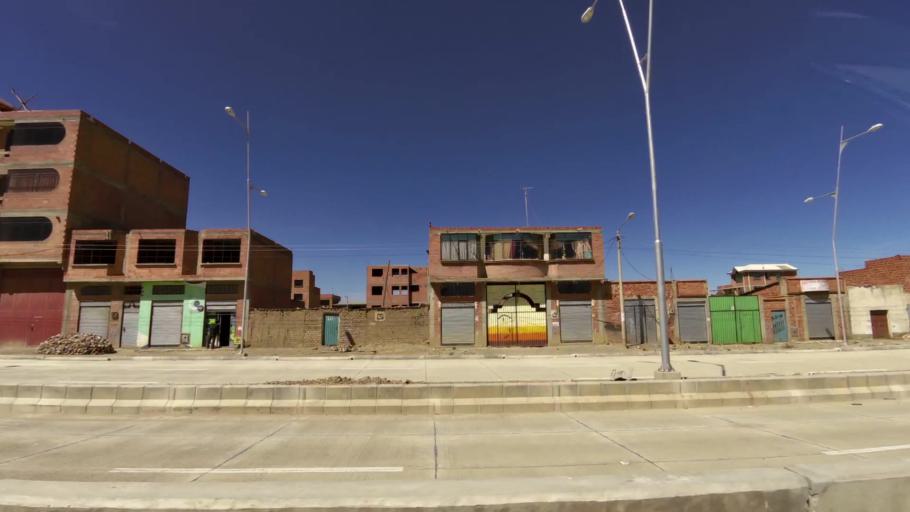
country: BO
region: La Paz
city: La Paz
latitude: -16.4952
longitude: -68.2224
